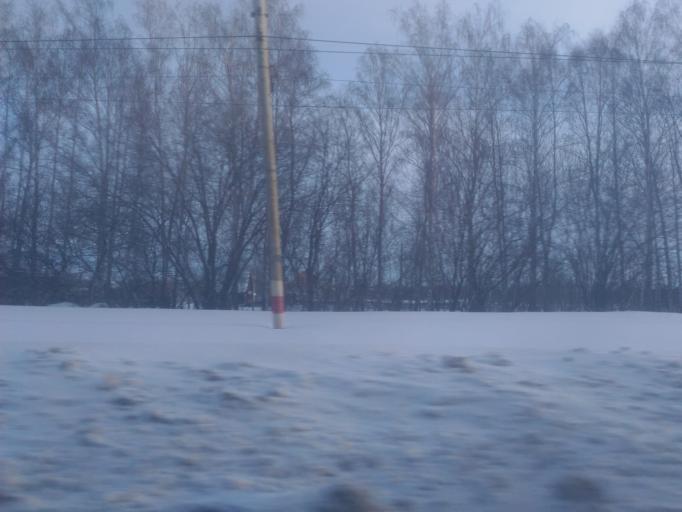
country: RU
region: Ulyanovsk
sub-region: Ulyanovskiy Rayon
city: Ulyanovsk
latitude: 54.3657
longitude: 48.3250
